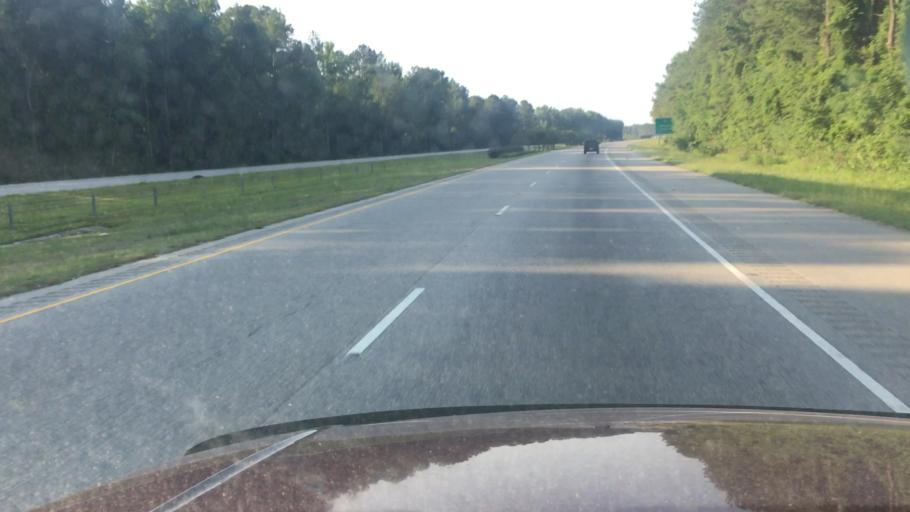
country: US
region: North Carolina
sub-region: Cumberland County
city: Fayetteville
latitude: 34.9961
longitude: -78.8633
